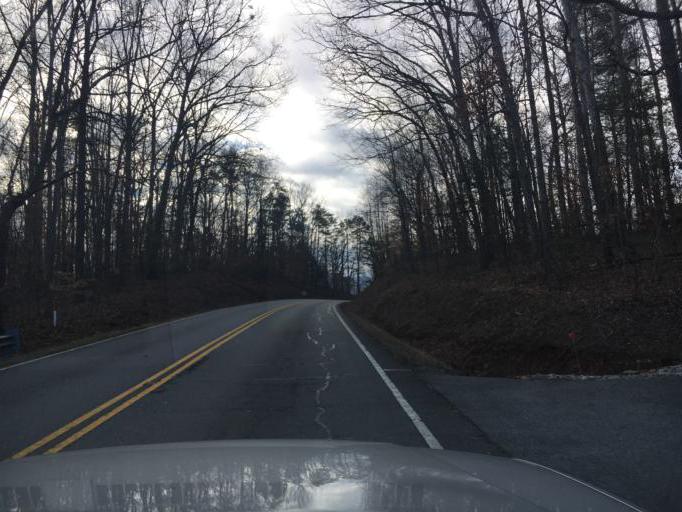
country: US
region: North Carolina
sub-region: Burke County
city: Salem
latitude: 35.6957
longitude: -81.7174
